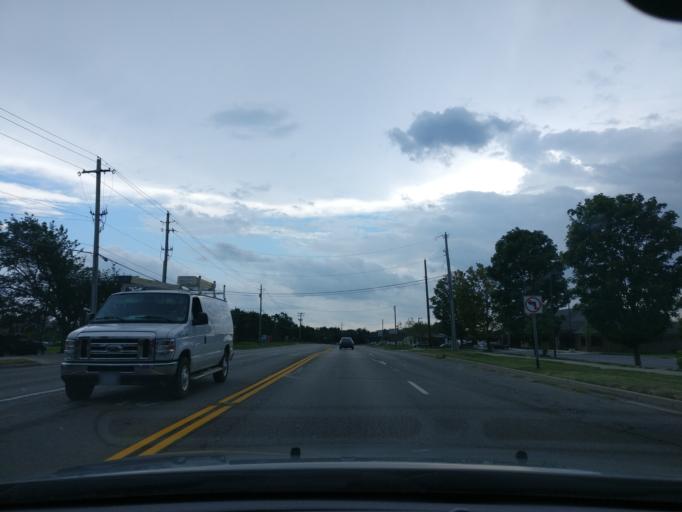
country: US
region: Ohio
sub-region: Montgomery County
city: Centerville
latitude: 39.6255
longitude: -84.1999
